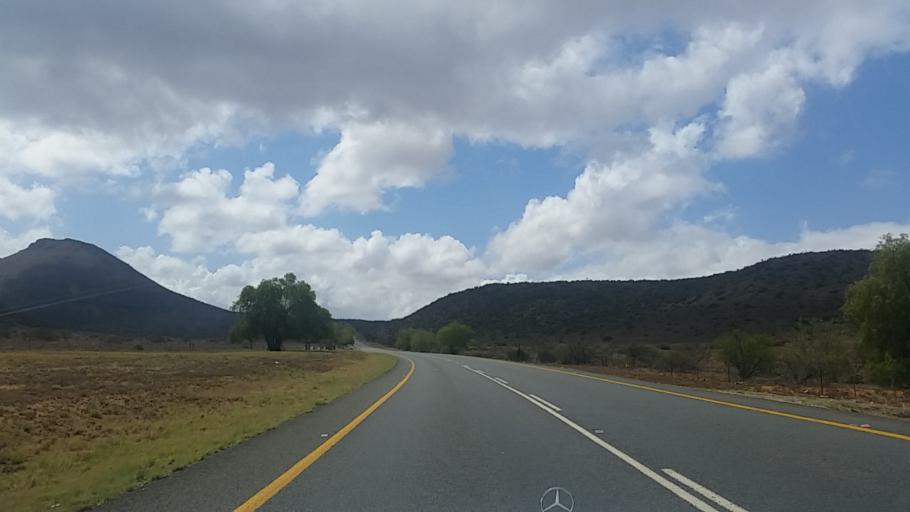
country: ZA
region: Eastern Cape
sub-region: Cacadu District Municipality
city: Graaff-Reinet
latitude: -32.0713
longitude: 24.6052
